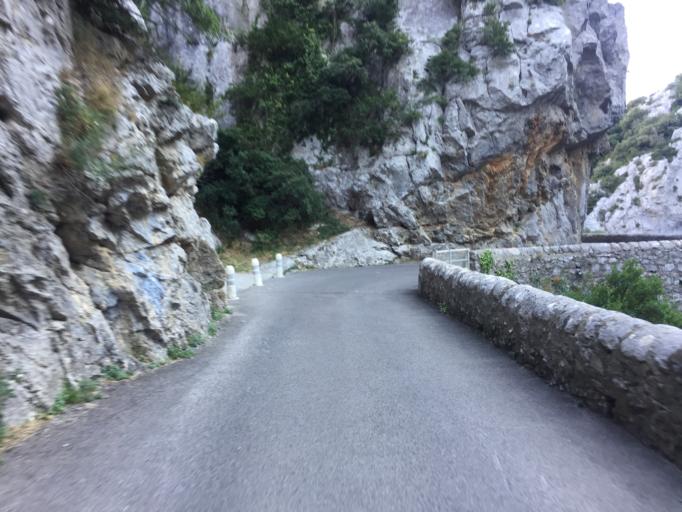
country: FR
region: Languedoc-Roussillon
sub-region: Departement des Pyrenees-Orientales
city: Saint-Paul-de-Fenouillet
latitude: 42.8392
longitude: 2.4799
